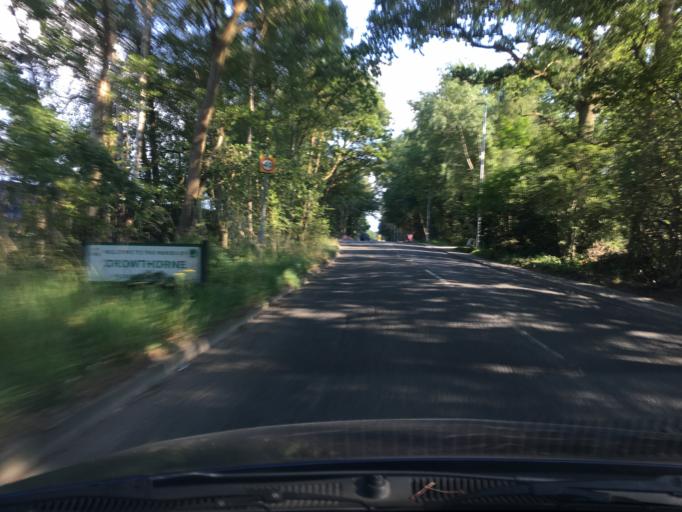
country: GB
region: England
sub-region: Bracknell Forest
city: Crowthorne
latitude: 51.3825
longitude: -0.7922
